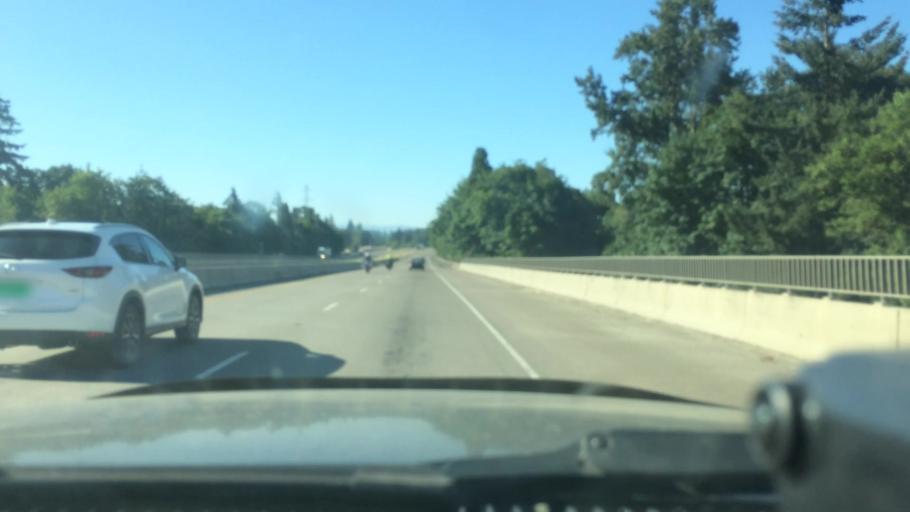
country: US
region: Oregon
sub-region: Lane County
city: Coburg
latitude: 44.1117
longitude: -123.0456
